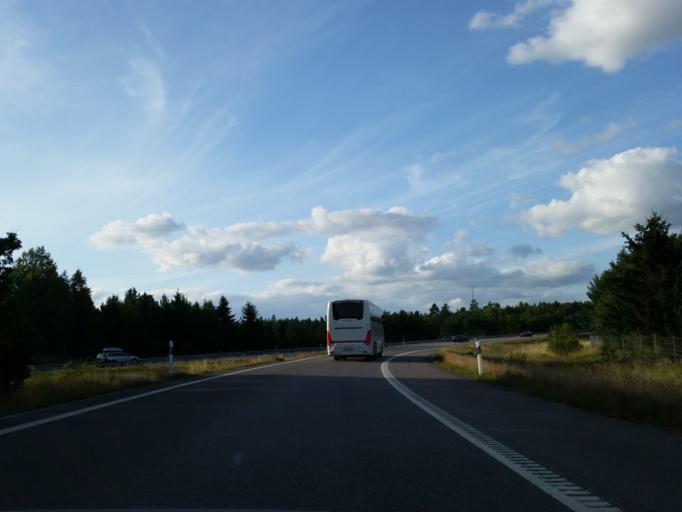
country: SE
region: Stockholm
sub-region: Sodertalje Kommun
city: Pershagen
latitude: 59.0896
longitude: 17.6008
